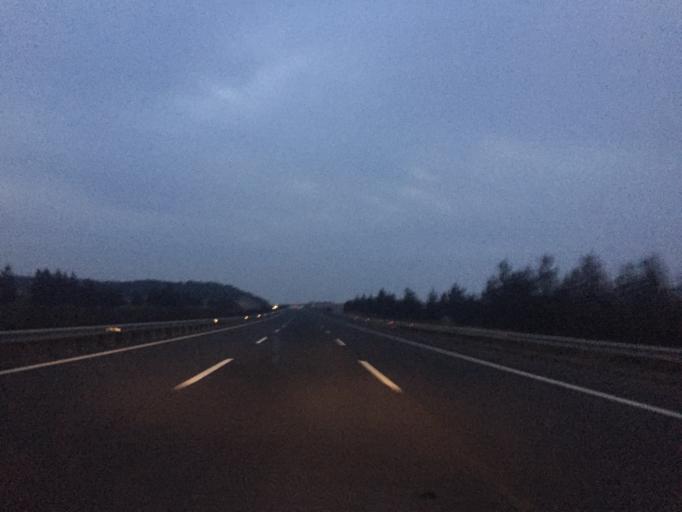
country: TR
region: Sanliurfa
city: Sanliurfa
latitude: 37.1975
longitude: 38.9245
